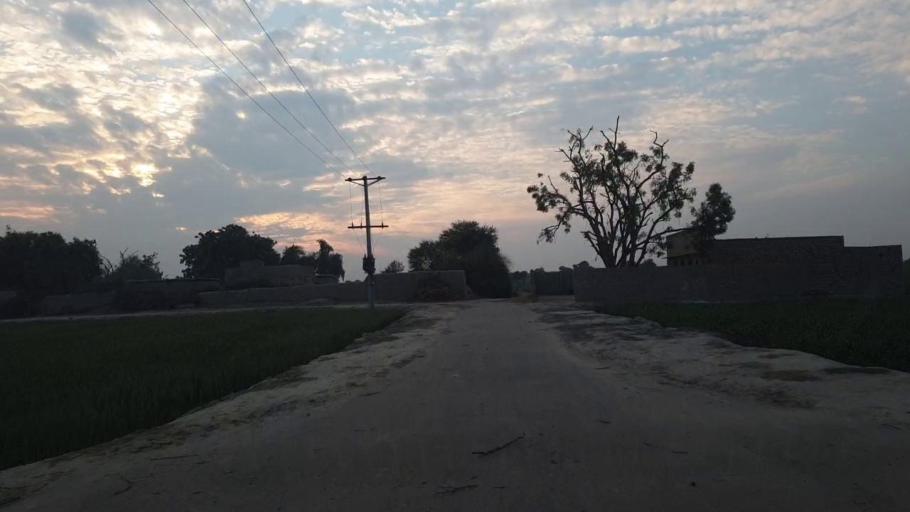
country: PK
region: Sindh
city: Shahpur Chakar
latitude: 26.0747
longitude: 68.5470
